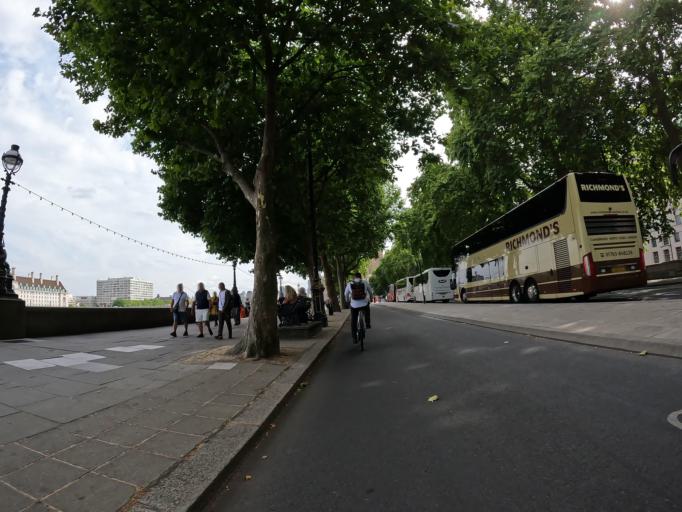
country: GB
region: England
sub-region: Greater London
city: Bromley
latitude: 51.4232
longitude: 0.0181
